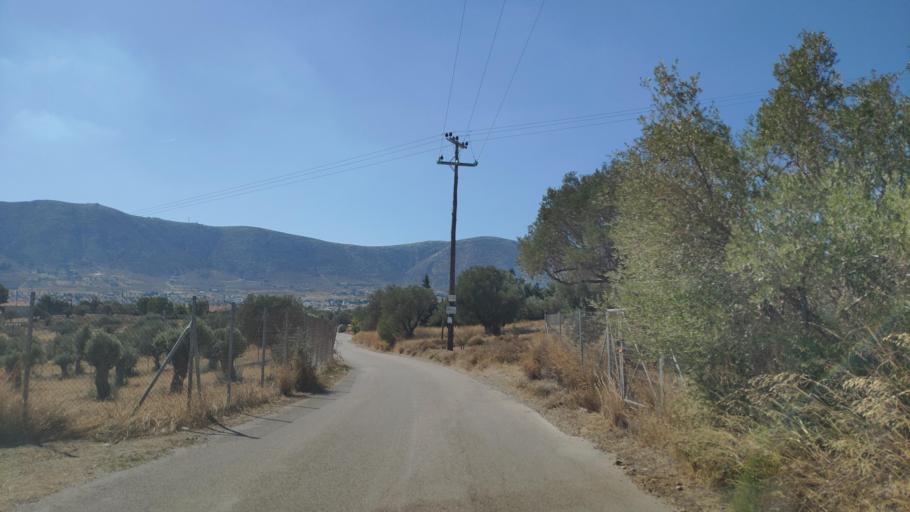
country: GR
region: Attica
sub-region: Nomarchia Anatolikis Attikis
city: Keratea
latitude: 37.8171
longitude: 23.9905
